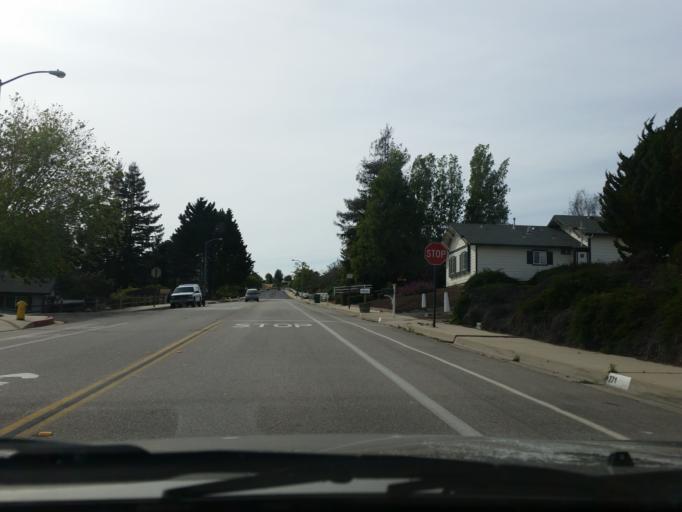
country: US
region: California
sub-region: San Luis Obispo County
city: Arroyo Grande
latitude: 35.1314
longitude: -120.5766
